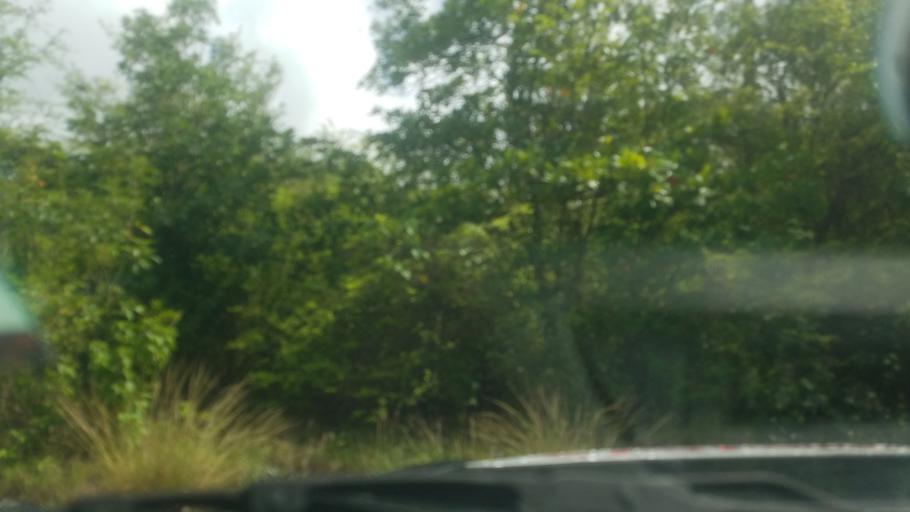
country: LC
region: Laborie Quarter
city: Laborie
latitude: 13.7421
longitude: -60.9730
